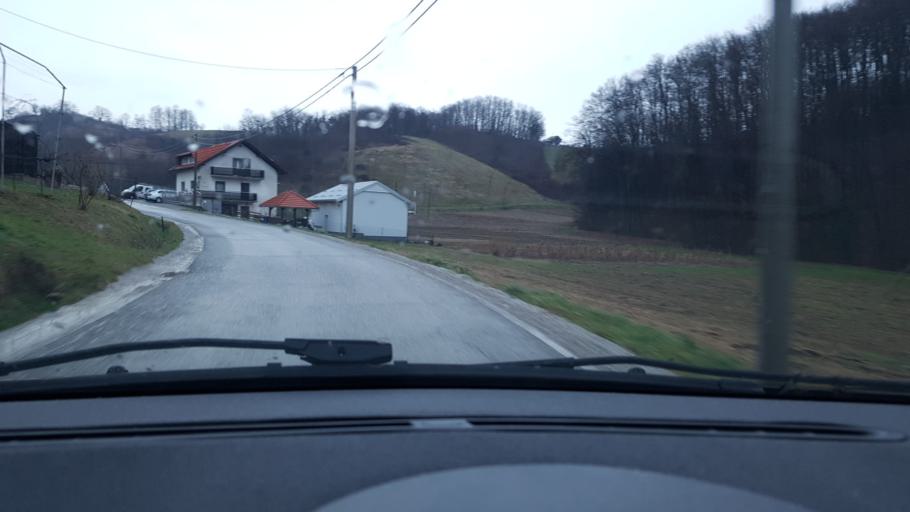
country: HR
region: Krapinsko-Zagorska
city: Bedekovcina
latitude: 45.9884
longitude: 15.9788
